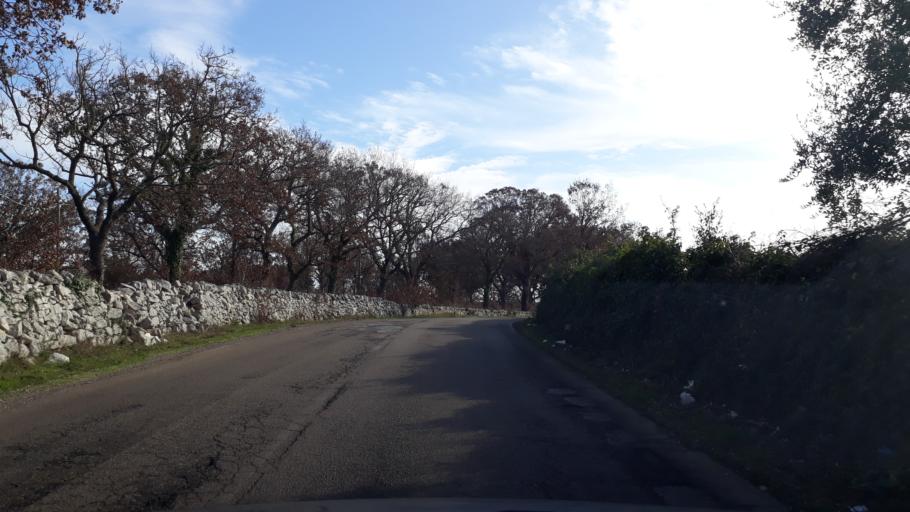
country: IT
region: Apulia
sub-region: Provincia di Taranto
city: Martina Franca
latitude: 40.6765
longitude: 17.3601
